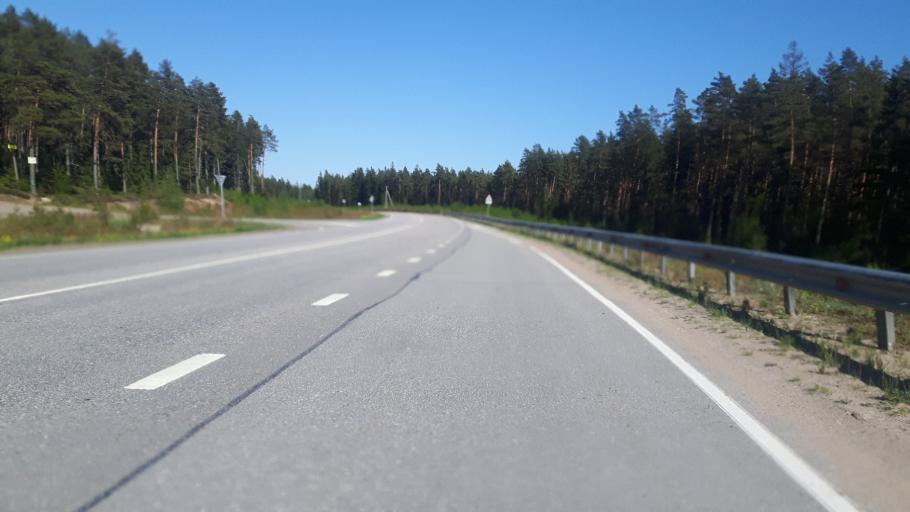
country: RU
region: Leningrad
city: Sosnovyy Bor
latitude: 60.1845
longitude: 29.0317
